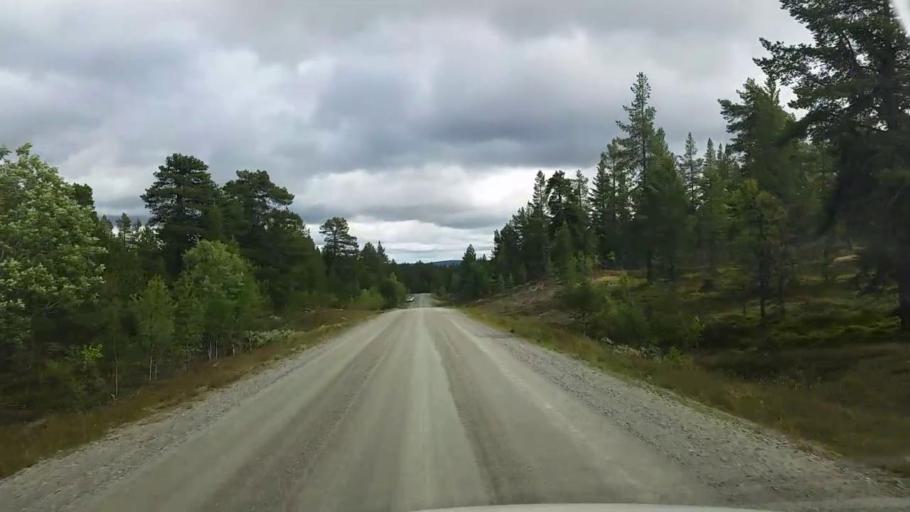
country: NO
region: Hedmark
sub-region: Engerdal
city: Engerdal
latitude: 62.3336
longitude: 12.6353
